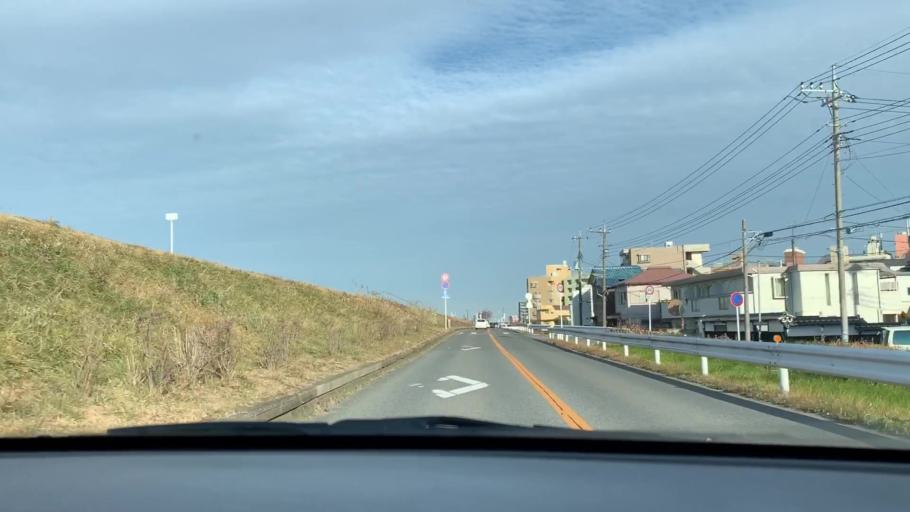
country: JP
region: Chiba
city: Matsudo
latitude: 35.7839
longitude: 139.8947
